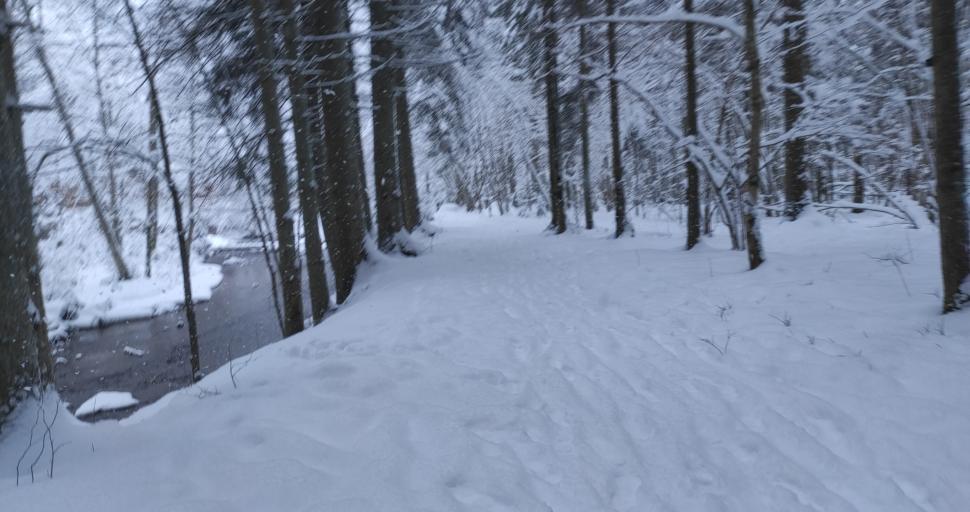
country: LV
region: Amatas Novads
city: Drabesi
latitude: 57.2191
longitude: 25.1621
